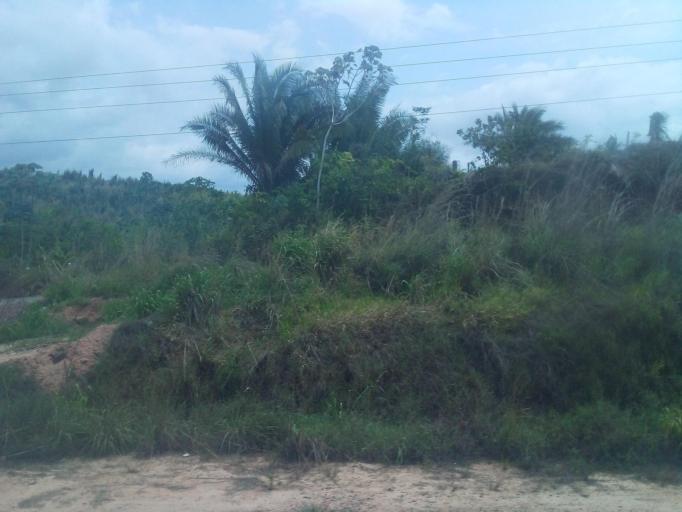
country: BR
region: Maranhao
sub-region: Santa Ines
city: Santa Ines
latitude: -3.7063
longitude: -45.9558
